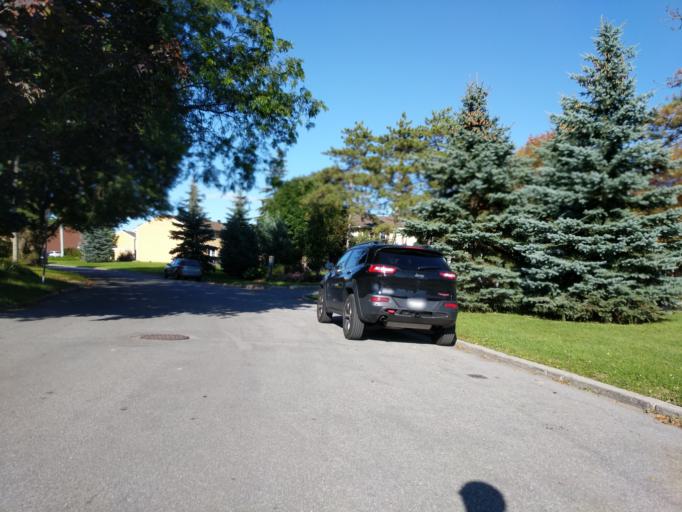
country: CA
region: Ontario
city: Ottawa
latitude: 45.3619
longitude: -75.7446
